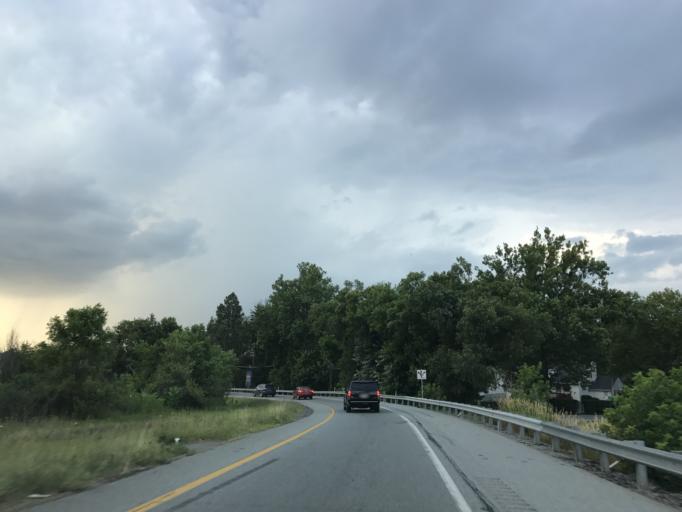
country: US
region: Pennsylvania
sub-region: York County
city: East York
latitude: 39.9708
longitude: -76.6921
